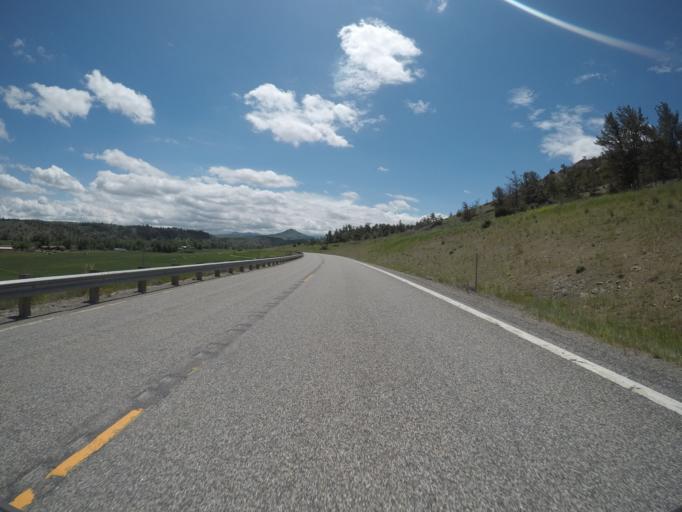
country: US
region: Montana
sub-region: Sweet Grass County
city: Big Timber
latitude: 45.7329
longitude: -109.9996
